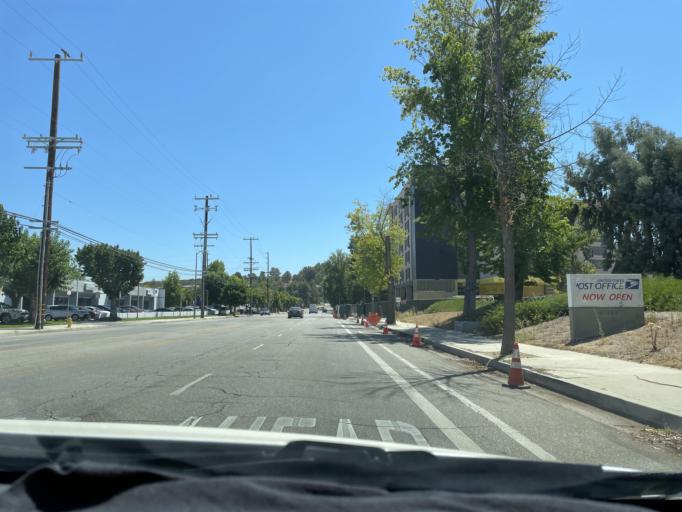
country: US
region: California
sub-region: Los Angeles County
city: Woodland Hills
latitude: 34.1792
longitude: -118.5944
